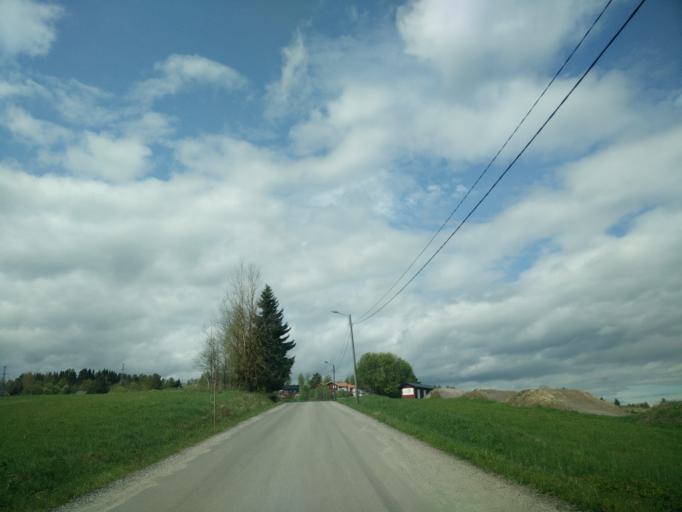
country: SE
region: Vaesternorrland
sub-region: Sundsvalls Kommun
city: Sundsvall
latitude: 62.3672
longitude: 17.2698
